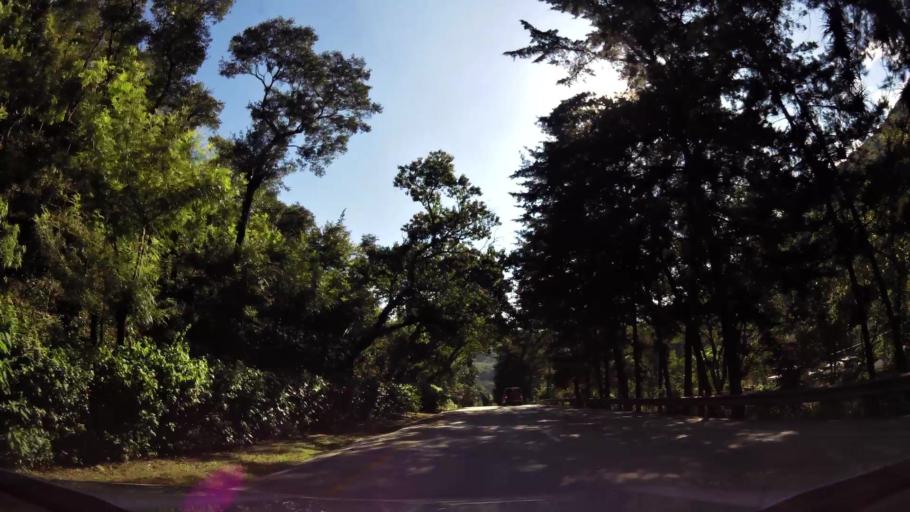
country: GT
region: Sacatepequez
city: Santa Lucia Milpas Altas
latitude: 14.5649
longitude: -90.7009
